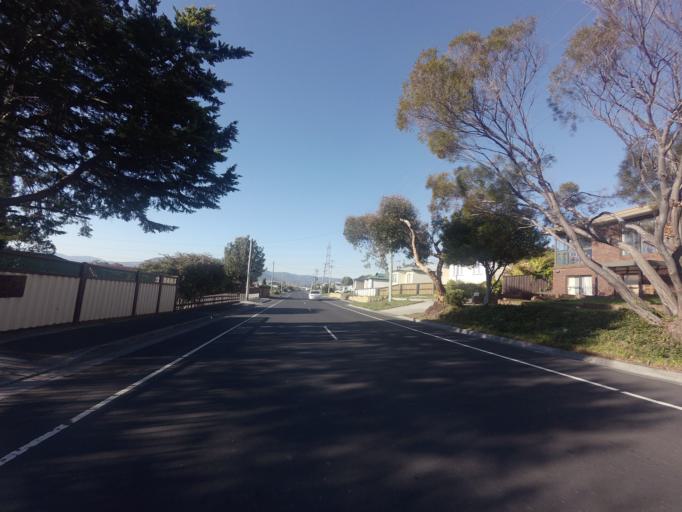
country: AU
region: Tasmania
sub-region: Glenorchy
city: Glenorchy
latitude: -42.8479
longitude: 147.2614
